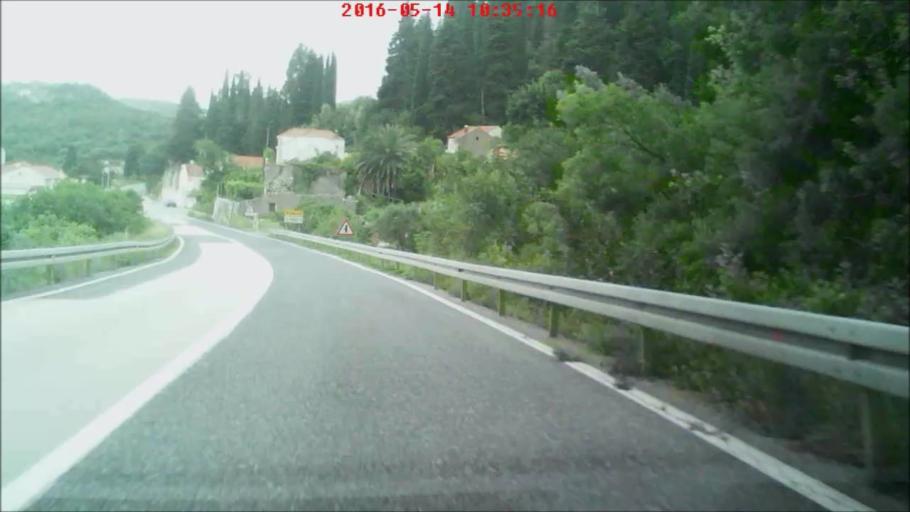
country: HR
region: Dubrovacko-Neretvanska
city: Podgora
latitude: 42.7878
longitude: 17.8936
